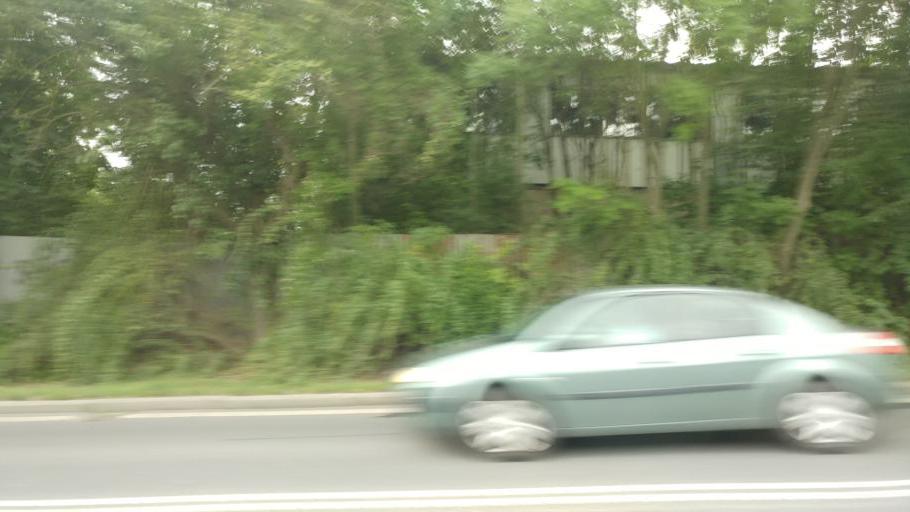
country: CZ
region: Central Bohemia
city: Roztoky
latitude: 50.1285
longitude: 14.3884
